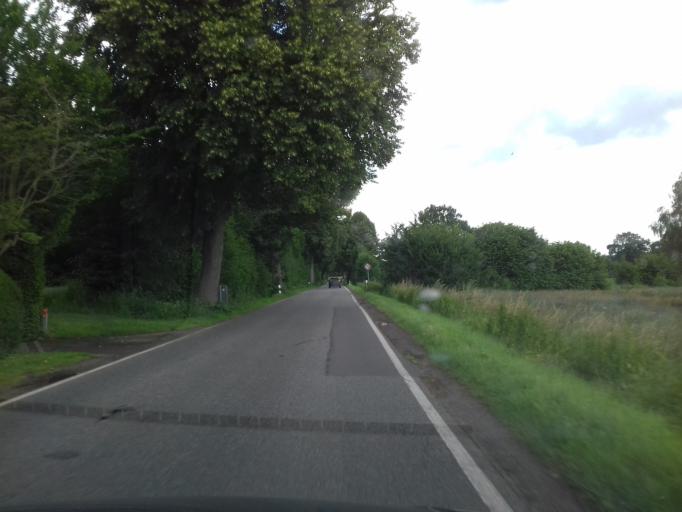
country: DE
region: Schleswig-Holstein
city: Elmenhorst
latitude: 53.7764
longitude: 10.2459
